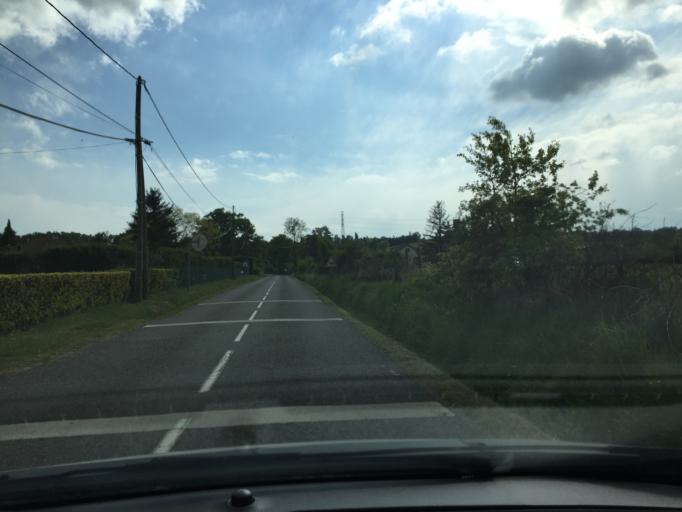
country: FR
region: Rhone-Alpes
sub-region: Departement du Rhone
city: Orlienas
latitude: 45.6528
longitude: 4.7042
